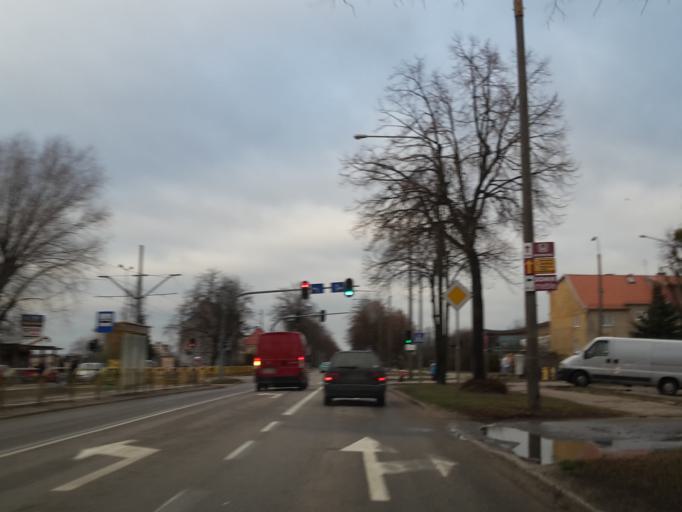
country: PL
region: Warmian-Masurian Voivodeship
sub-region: Powiat elblaski
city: Gronowo Gorne
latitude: 54.1466
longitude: 19.4352
